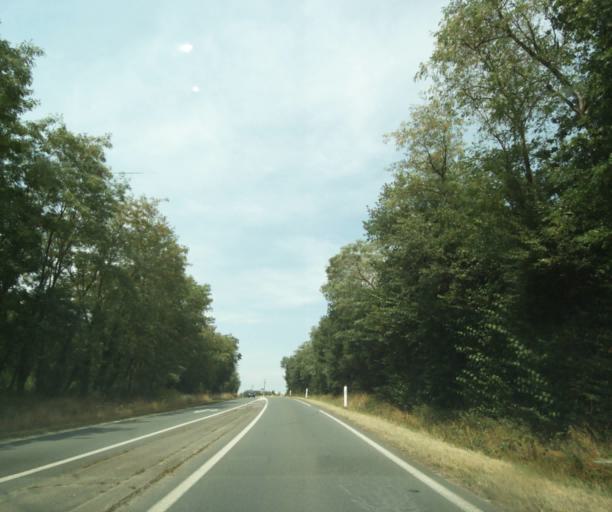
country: FR
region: Poitou-Charentes
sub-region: Departement de la Vienne
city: Cenon-sur-Vienne
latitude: 46.7515
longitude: 0.5548
